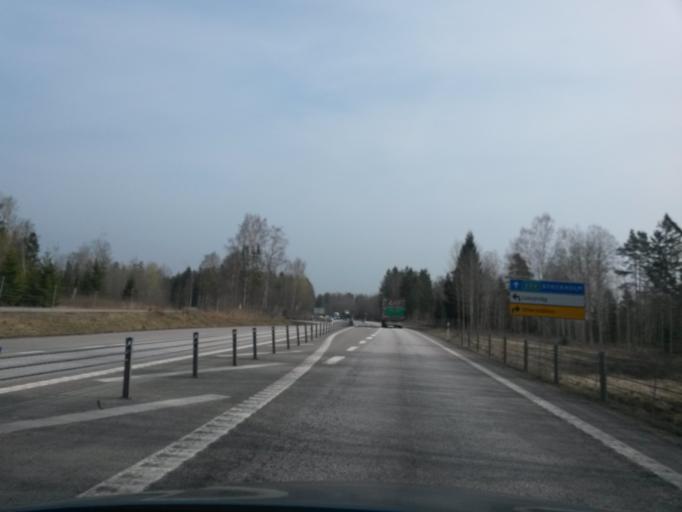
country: SE
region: Vaestra Goetaland
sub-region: Gullspangs Kommun
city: Hova
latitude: 58.8113
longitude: 14.1279
